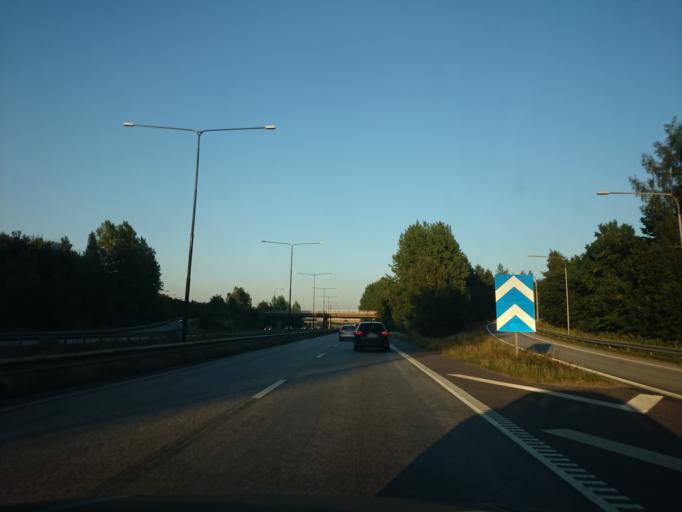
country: SE
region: Skane
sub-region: Malmo
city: Malmoe
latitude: 55.5640
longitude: 13.0236
